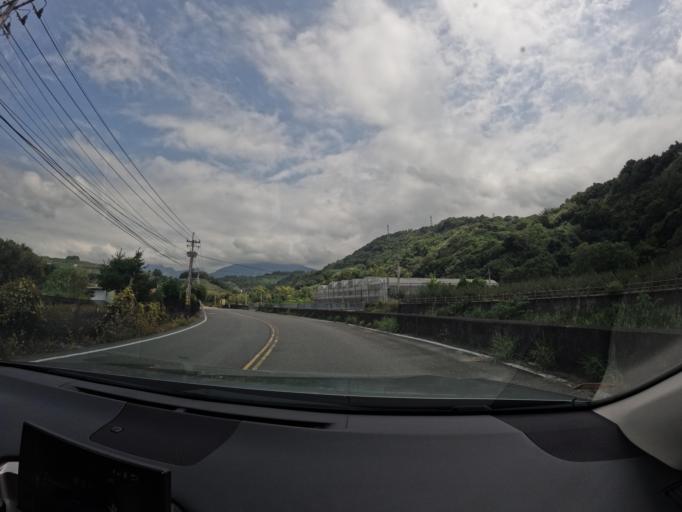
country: TW
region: Taiwan
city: Fengyuan
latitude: 24.3070
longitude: 120.8482
